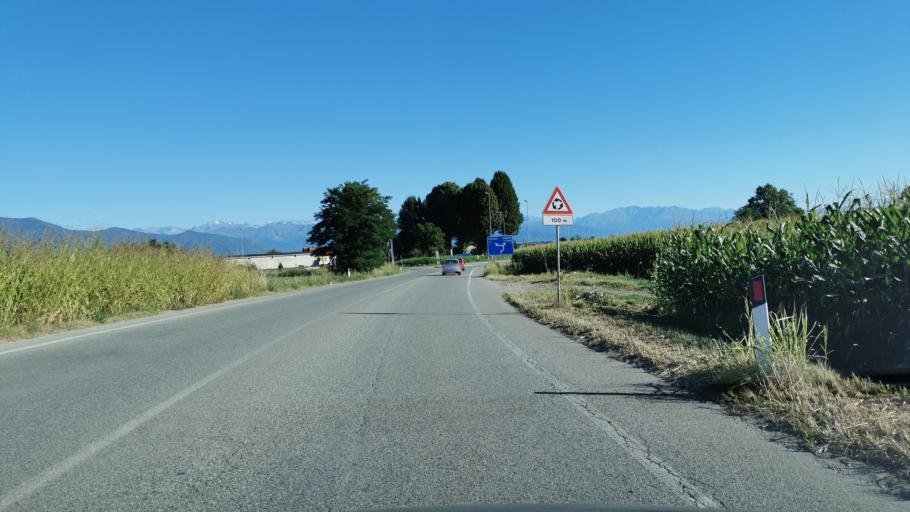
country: IT
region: Piedmont
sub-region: Provincia di Torino
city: Druento
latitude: 45.1156
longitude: 7.5904
